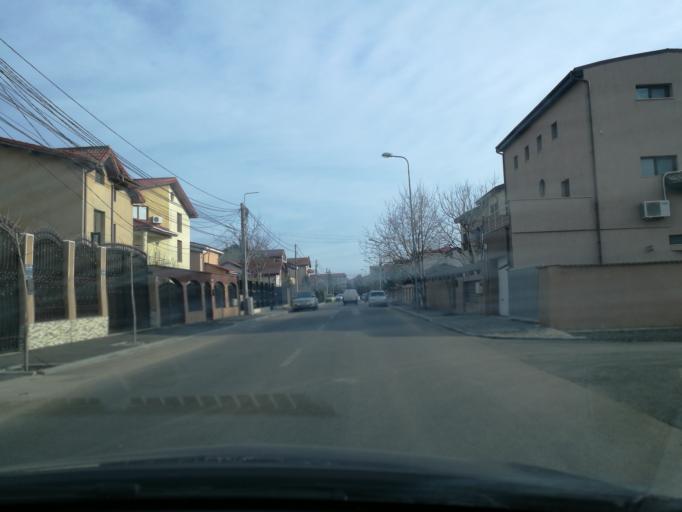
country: RO
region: Constanta
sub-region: Municipiul Constanta
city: Constanta
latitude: 44.1807
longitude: 28.6122
